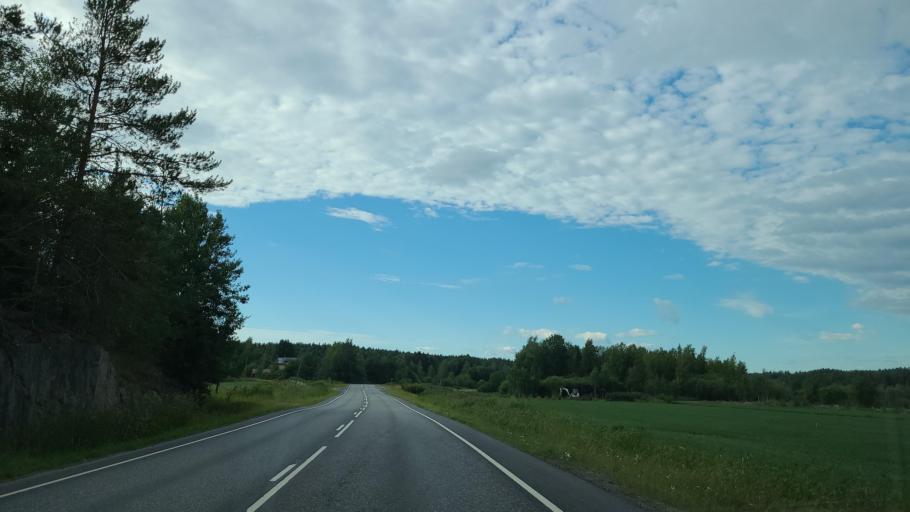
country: FI
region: Varsinais-Suomi
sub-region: Turku
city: Merimasku
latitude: 60.4270
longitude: 21.8966
